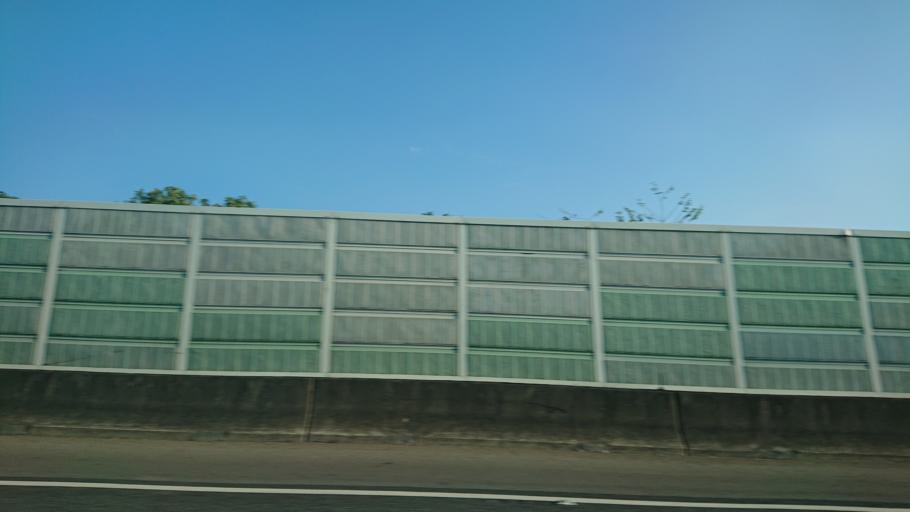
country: TW
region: Taiwan
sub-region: Changhua
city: Chang-hua
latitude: 24.1155
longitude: 120.6123
